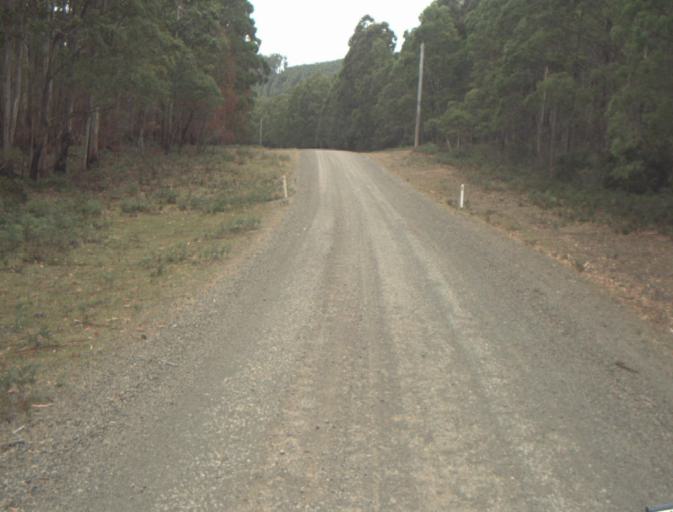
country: AU
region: Tasmania
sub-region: Dorset
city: Scottsdale
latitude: -41.4376
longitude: 147.5149
